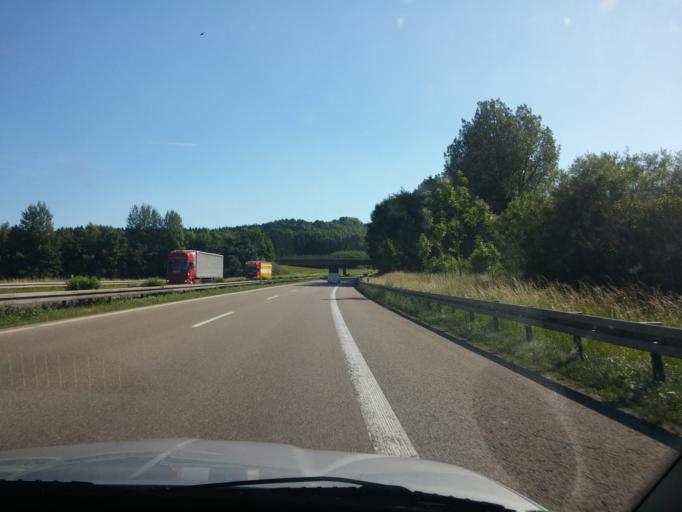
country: DE
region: Baden-Wuerttemberg
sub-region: Tuebingen Region
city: Aichstetten
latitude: 47.9030
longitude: 10.0639
